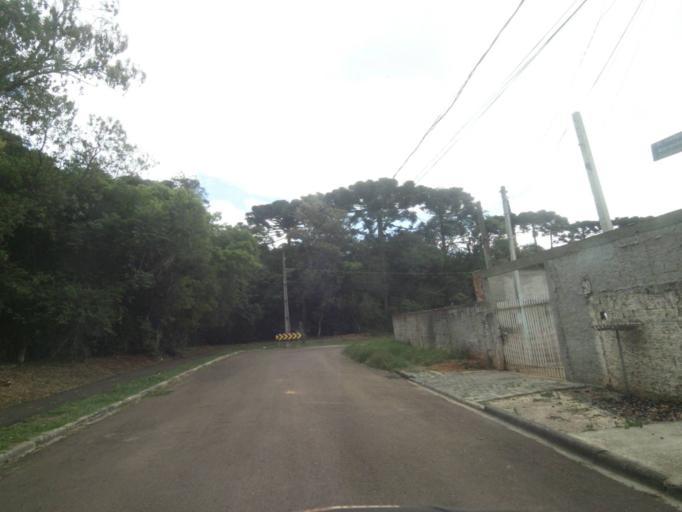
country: BR
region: Parana
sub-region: Sao Jose Dos Pinhais
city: Sao Jose dos Pinhais
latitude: -25.5560
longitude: -49.2604
